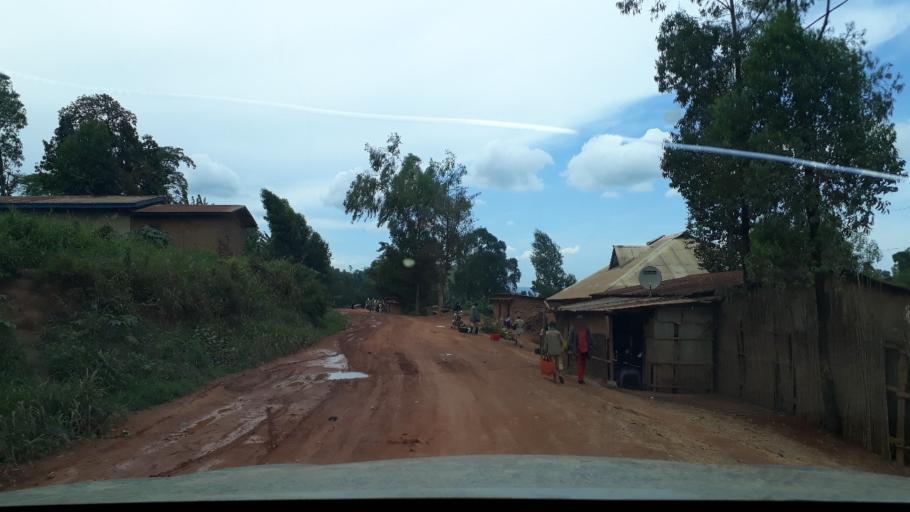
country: CD
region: Eastern Province
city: Bunia
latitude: 1.7396
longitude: 30.3437
